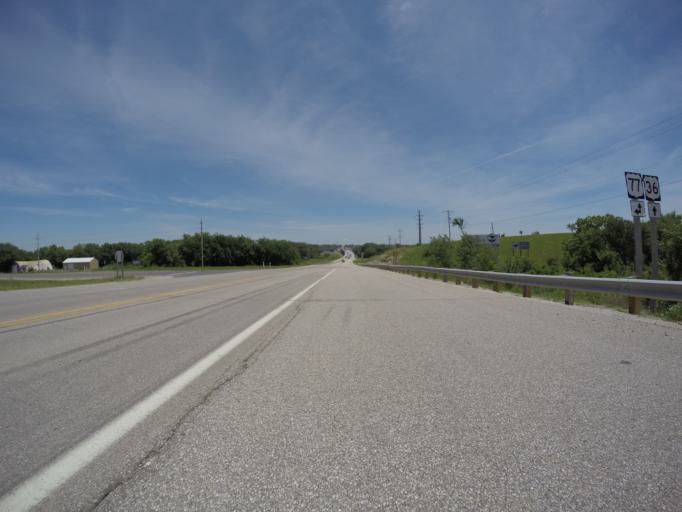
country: US
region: Kansas
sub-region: Marshall County
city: Marysville
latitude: 39.8422
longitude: -96.6671
